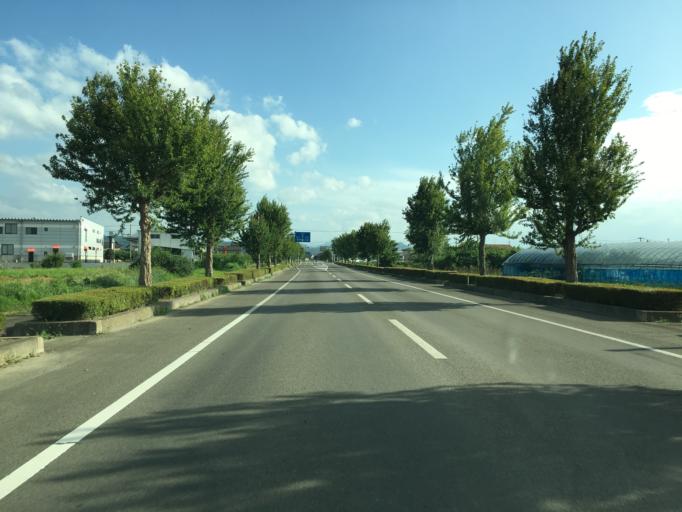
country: JP
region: Fukushima
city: Yanagawamachi-saiwaicho
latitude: 37.8521
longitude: 140.5926
